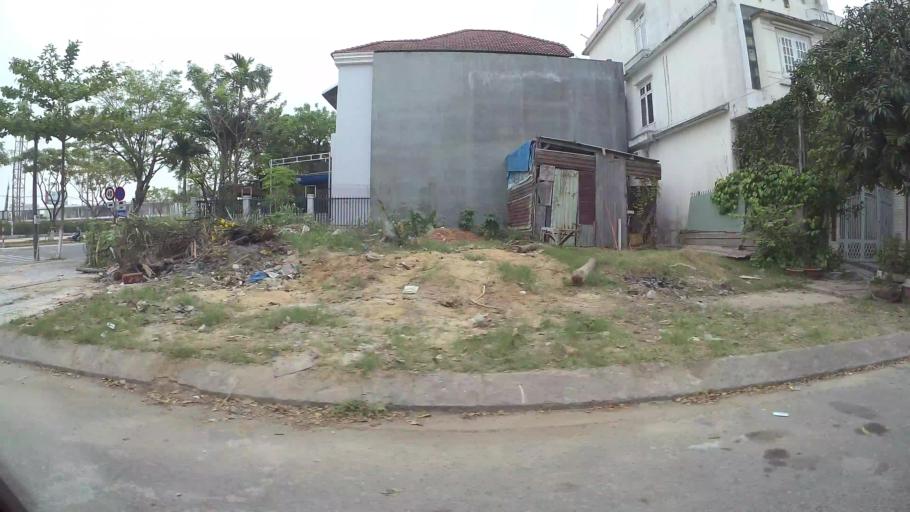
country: VN
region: Da Nang
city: Cam Le
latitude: 16.0250
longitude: 108.2151
